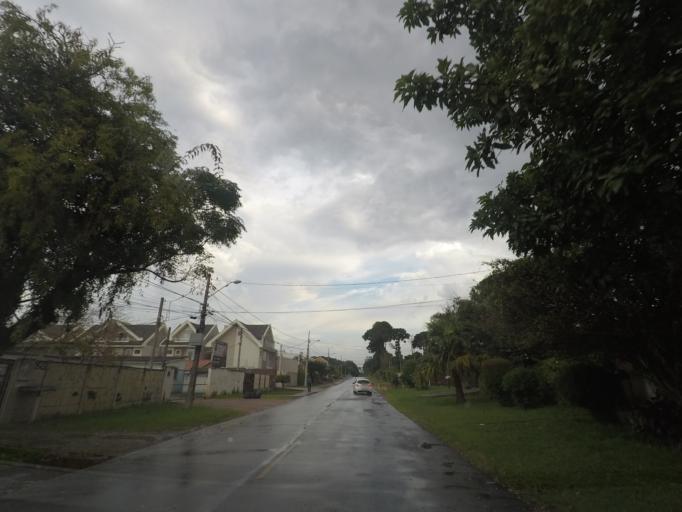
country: BR
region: Parana
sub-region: Sao Jose Dos Pinhais
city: Sao Jose dos Pinhais
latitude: -25.4945
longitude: -49.2464
